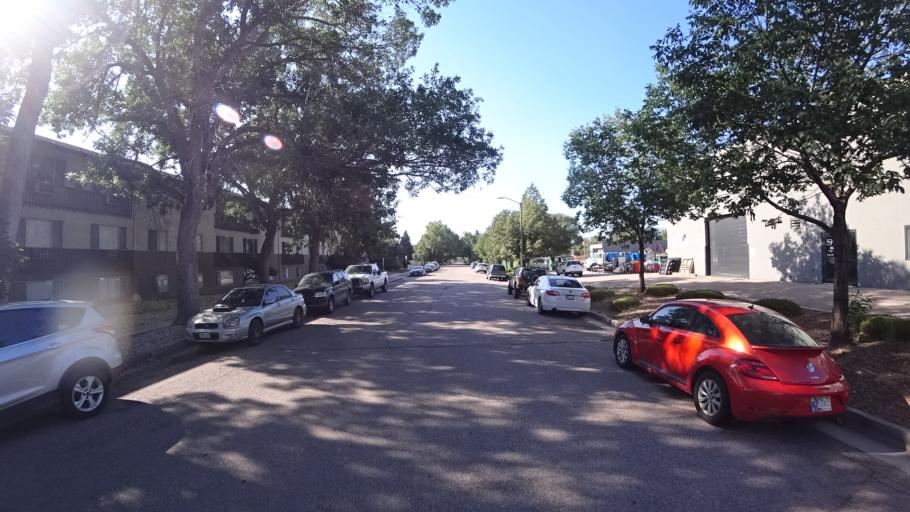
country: US
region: Colorado
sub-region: El Paso County
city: Colorado Springs
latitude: 38.8745
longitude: -104.8283
